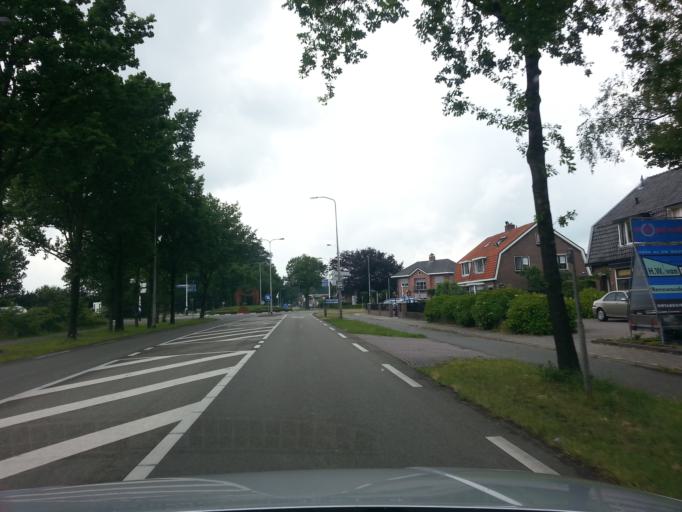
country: NL
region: Gelderland
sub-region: Gemeente Ede
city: Ederveen
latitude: 52.0755
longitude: 5.5325
